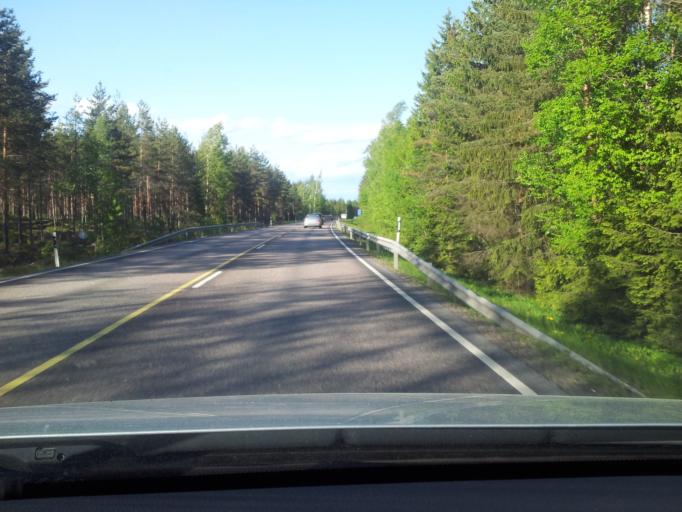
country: FI
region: Kymenlaakso
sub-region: Kouvola
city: Kouvola
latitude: 60.8543
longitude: 26.5498
